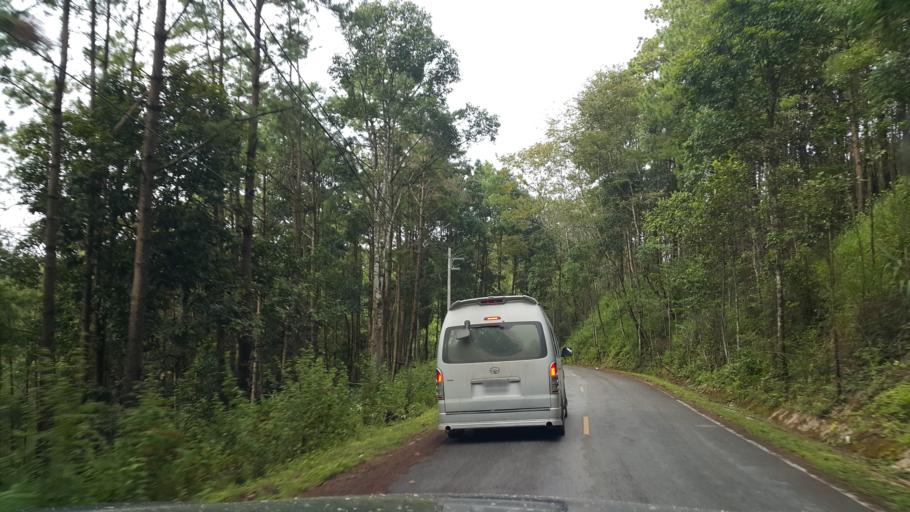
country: TH
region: Chiang Mai
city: Chaem Luang
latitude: 18.9257
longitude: 98.4774
